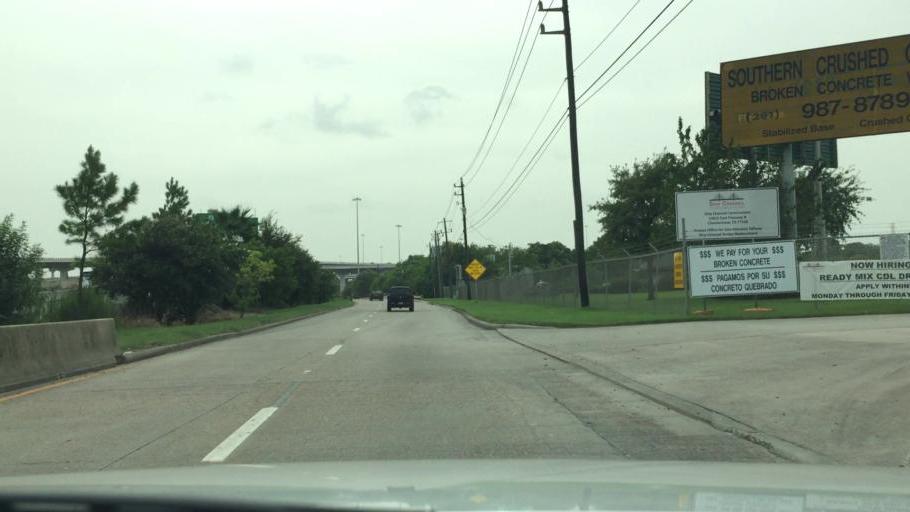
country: US
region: Texas
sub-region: Harris County
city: Cloverleaf
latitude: 29.7730
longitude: -95.1477
